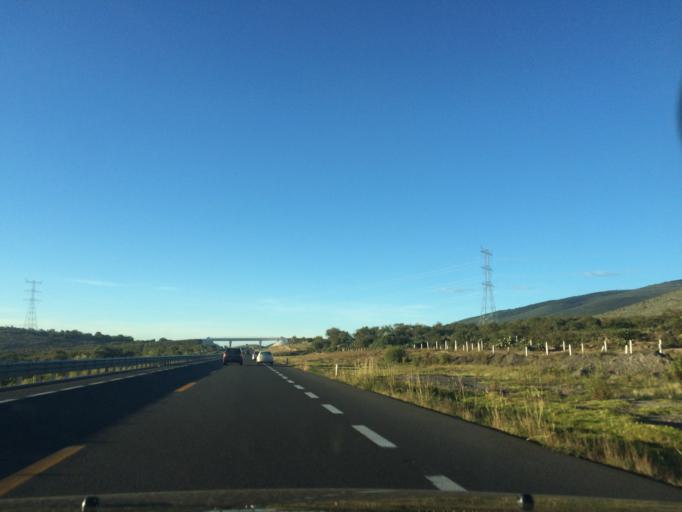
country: MX
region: Puebla
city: Morelos Canada
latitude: 18.7066
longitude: -97.4678
